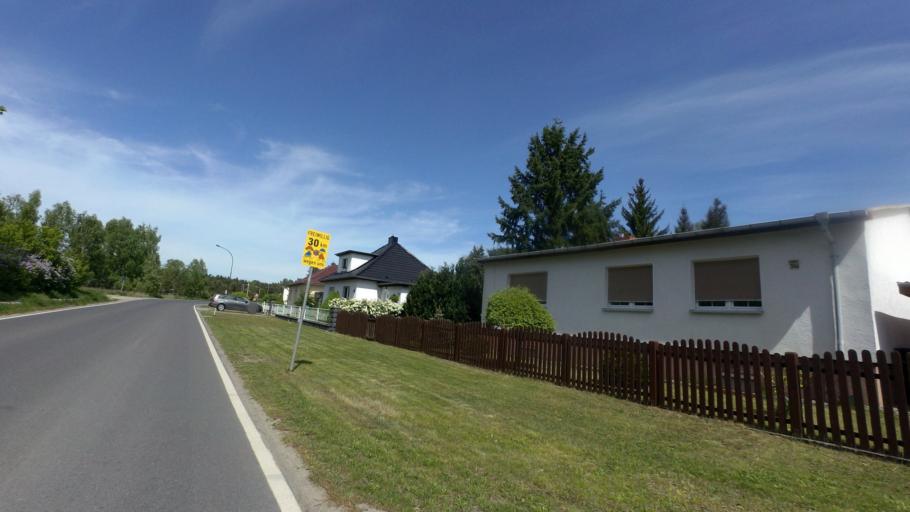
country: DE
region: Brandenburg
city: Sperenberg
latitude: 52.1469
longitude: 13.3651
